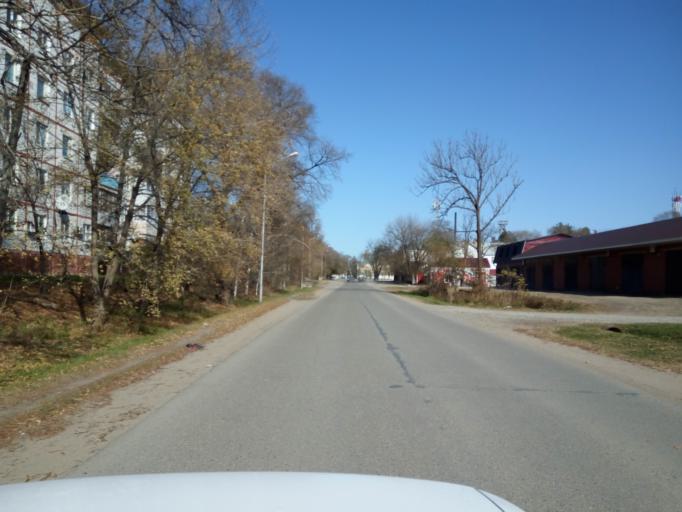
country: RU
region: Primorskiy
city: Dal'nerechensk
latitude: 45.9306
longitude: 133.7238
